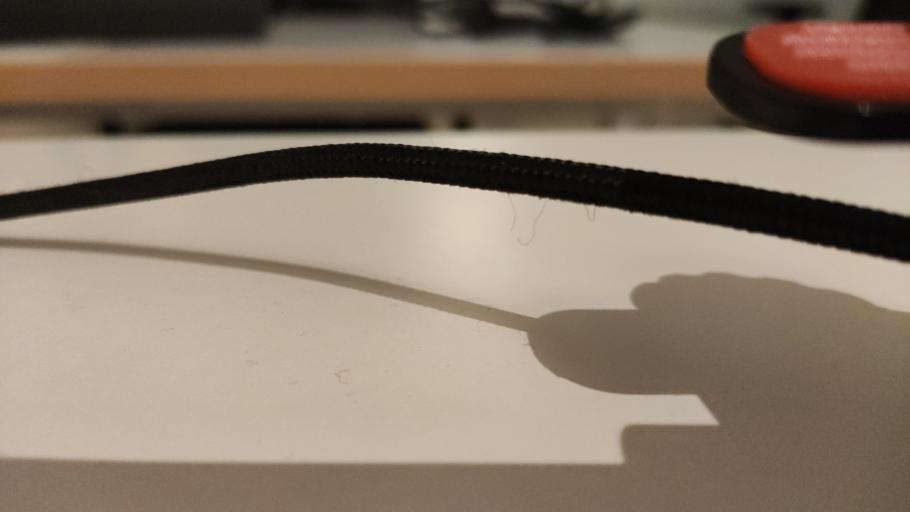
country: RU
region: Moskovskaya
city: Novoye
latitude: 55.6119
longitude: 38.9332
